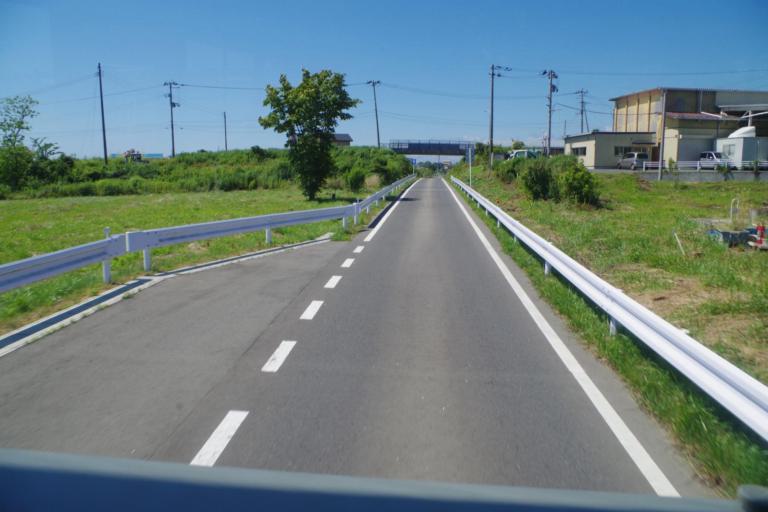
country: JP
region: Iwate
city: Ofunato
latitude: 38.8286
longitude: 141.5784
